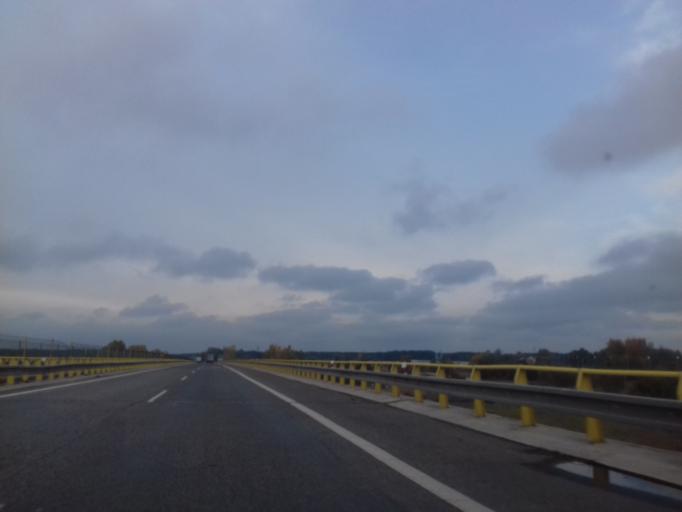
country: AT
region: Lower Austria
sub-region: Politischer Bezirk Mistelbach
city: Rabensburg
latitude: 48.6025
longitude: 17.0157
